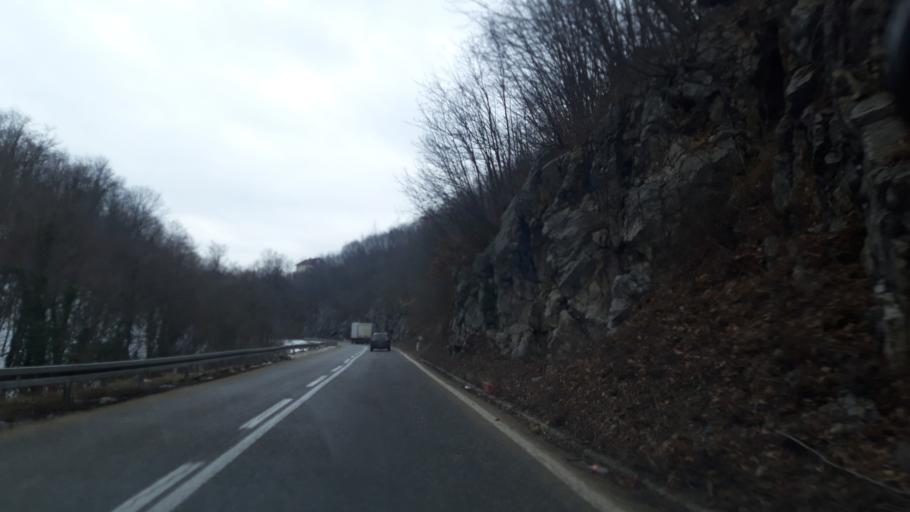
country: BA
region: Republika Srpska
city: Vlasenica
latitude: 44.1831
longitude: 18.9749
